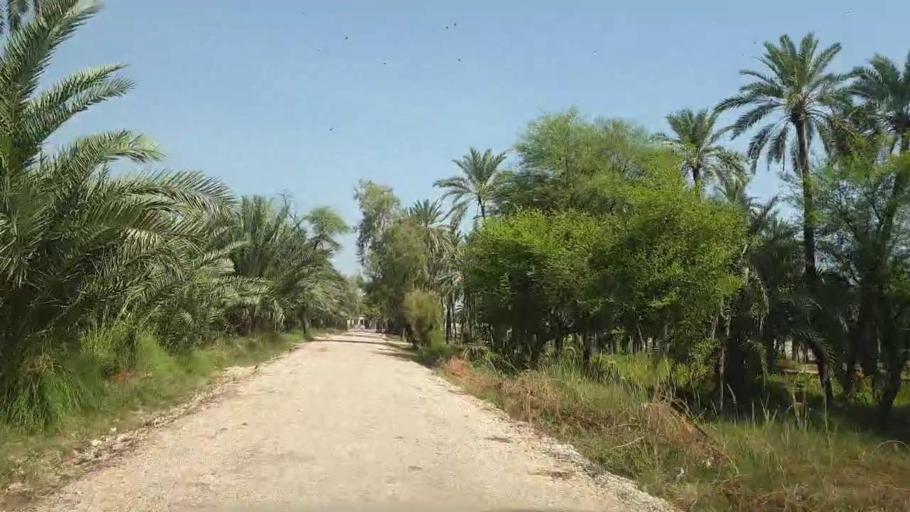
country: PK
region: Sindh
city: Rohri
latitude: 27.6950
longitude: 68.9468
